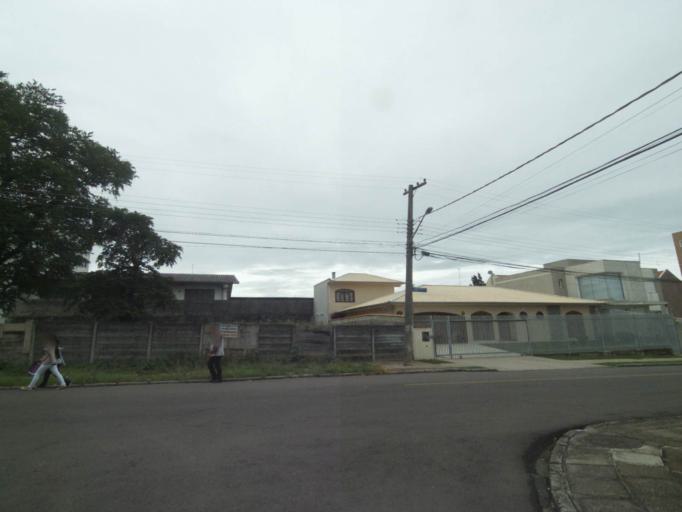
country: BR
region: Parana
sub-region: Curitiba
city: Curitiba
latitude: -25.4899
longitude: -49.2902
